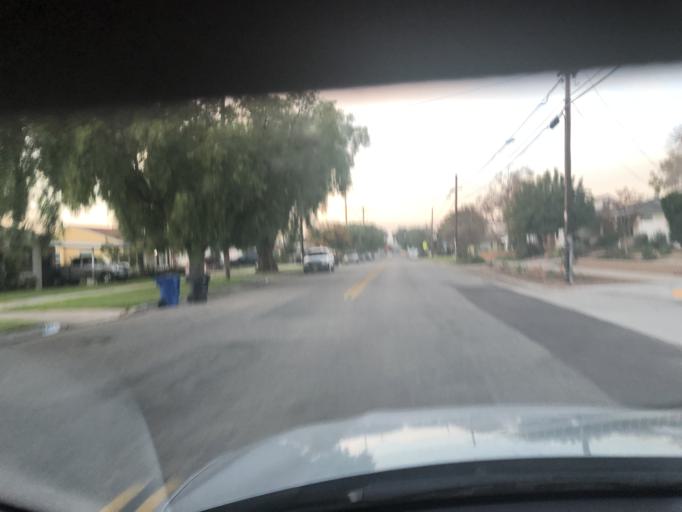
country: US
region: California
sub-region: San Diego County
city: Chula Vista
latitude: 32.6442
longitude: -117.0719
